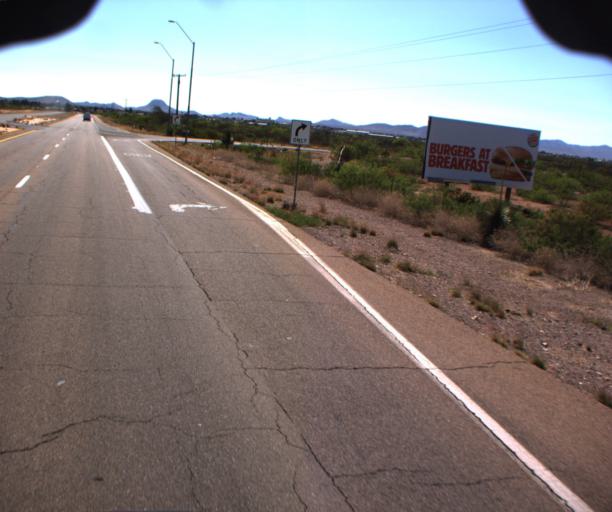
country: US
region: Arizona
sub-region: Cochise County
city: Pirtleville
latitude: 31.3516
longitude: -109.5731
